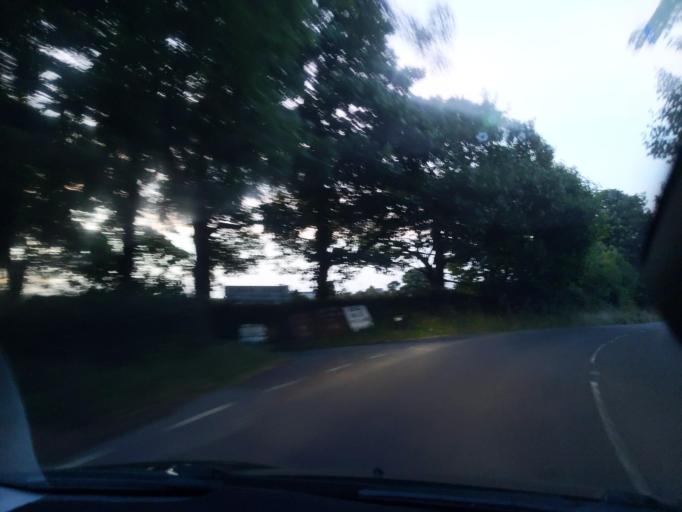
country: GB
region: England
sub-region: Cornwall
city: Camborne
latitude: 50.2028
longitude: -5.3048
